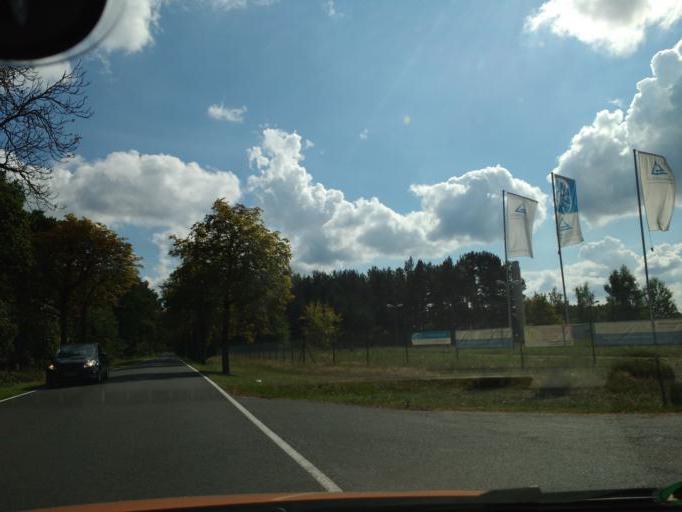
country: DE
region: Brandenburg
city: Oranienburg
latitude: 52.7410
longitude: 13.2723
